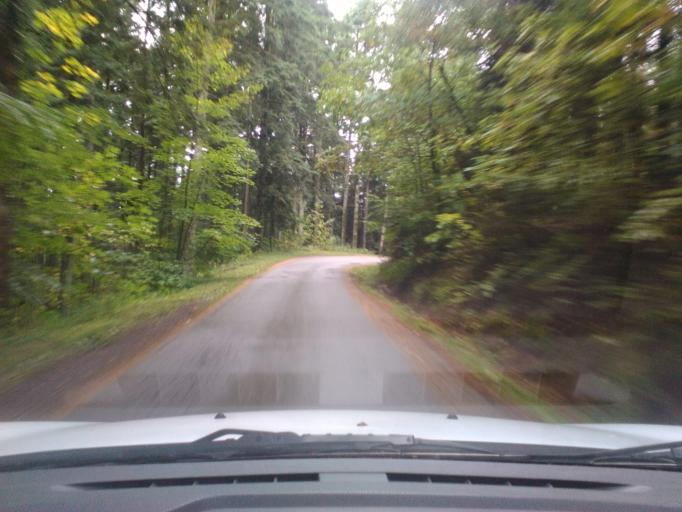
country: FR
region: Lorraine
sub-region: Departement des Vosges
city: Sainte-Marguerite
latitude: 48.2968
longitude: 6.9849
